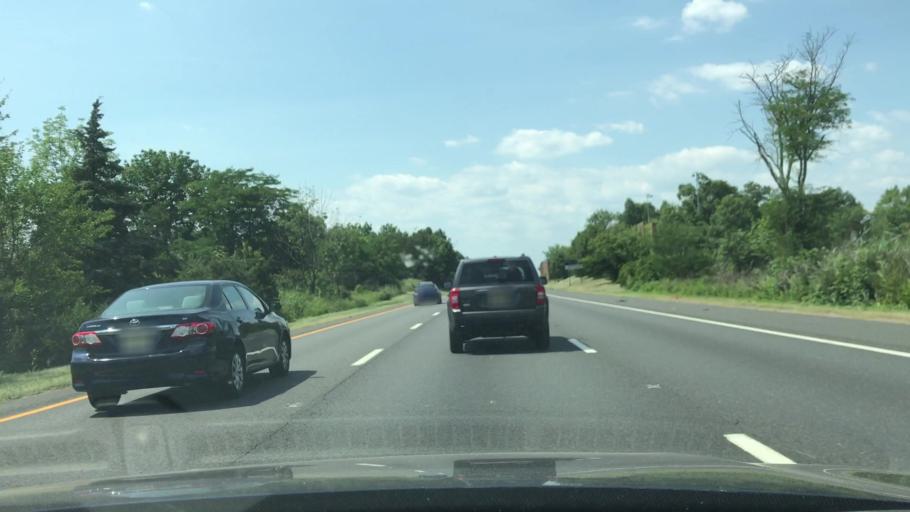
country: US
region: New Jersey
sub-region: Somerset County
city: Green Knoll
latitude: 40.5882
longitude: -74.6162
